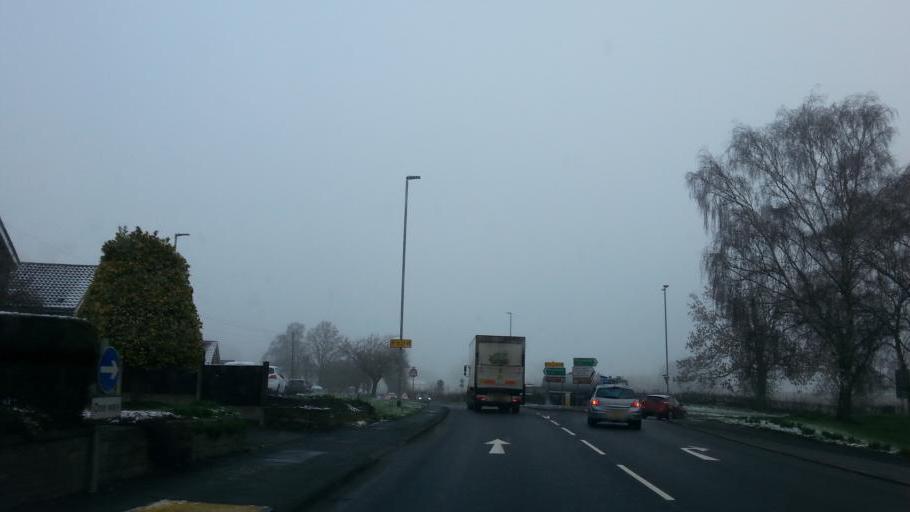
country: GB
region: England
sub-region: Cheshire East
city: Congleton
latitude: 53.1740
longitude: -2.2082
